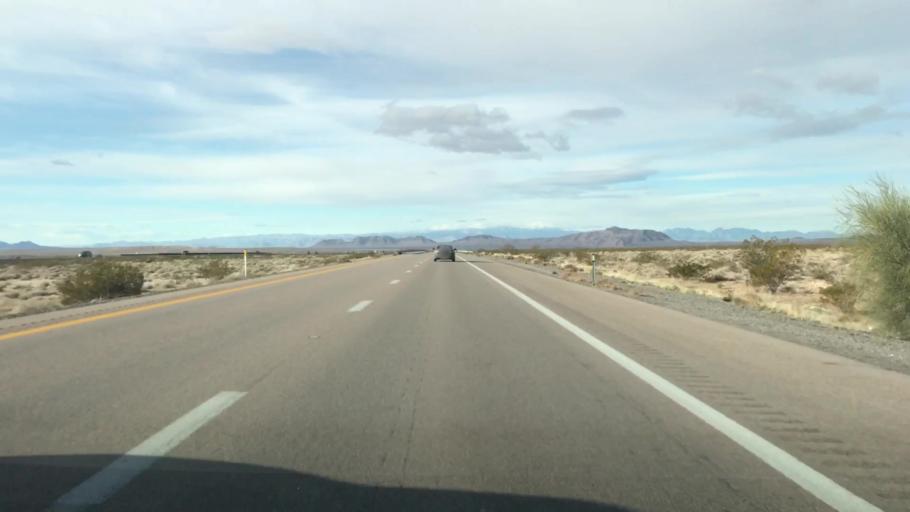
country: US
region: Nevada
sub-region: Clark County
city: Bunkerville
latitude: 36.7704
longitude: -114.3147
